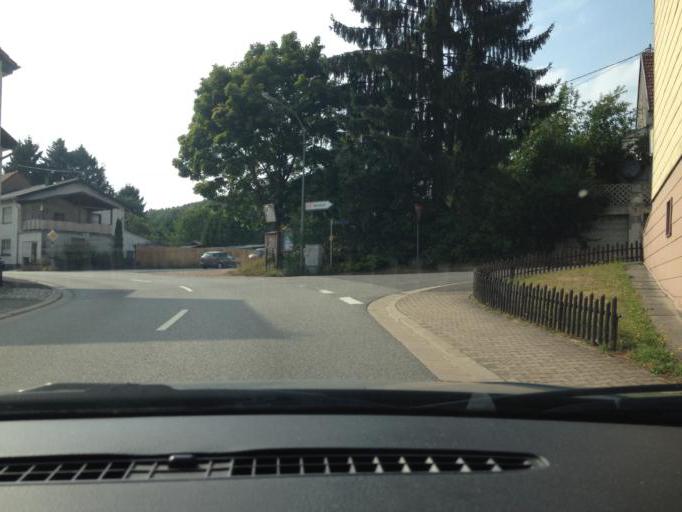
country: DE
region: Saarland
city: Namborn
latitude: 49.5216
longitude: 7.1440
